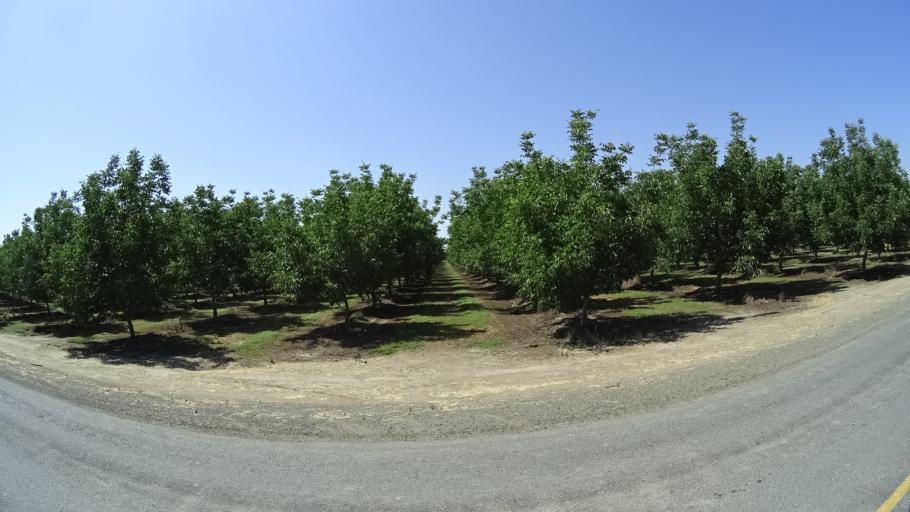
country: US
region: California
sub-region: Kings County
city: Lucerne
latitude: 36.3717
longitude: -119.6929
